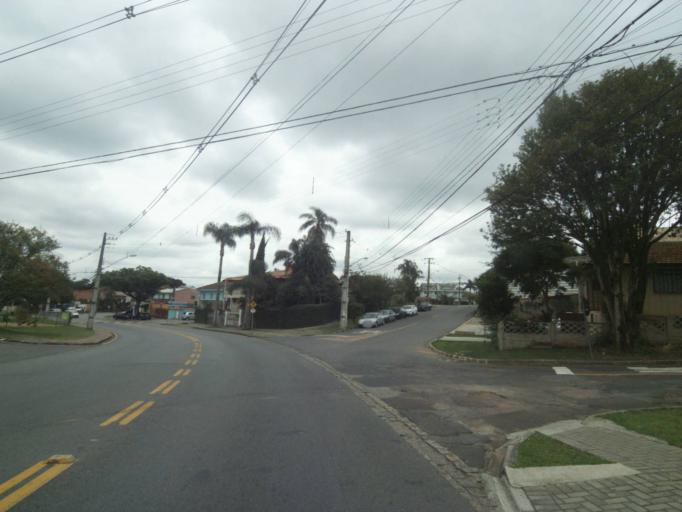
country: BR
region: Parana
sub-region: Curitiba
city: Curitiba
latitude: -25.3955
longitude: -49.2880
